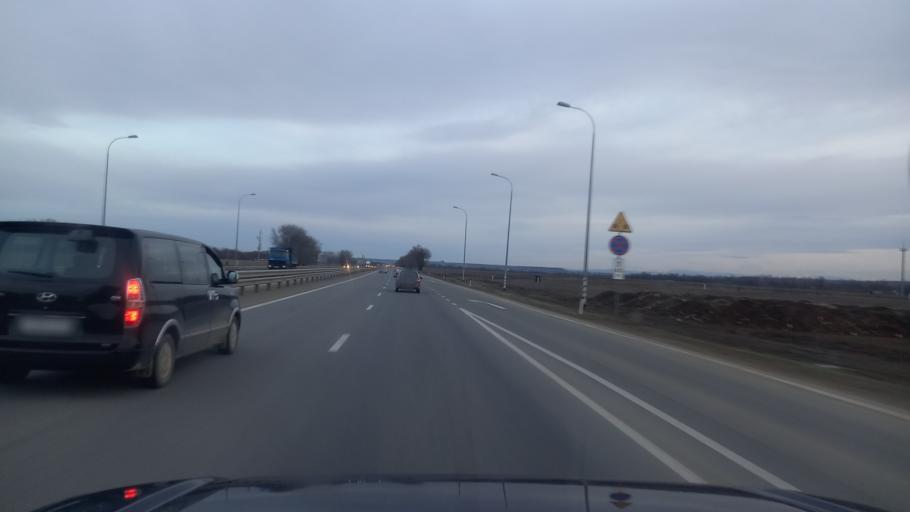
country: RU
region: Adygeya
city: Khanskaya
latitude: 44.6568
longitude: 39.9972
